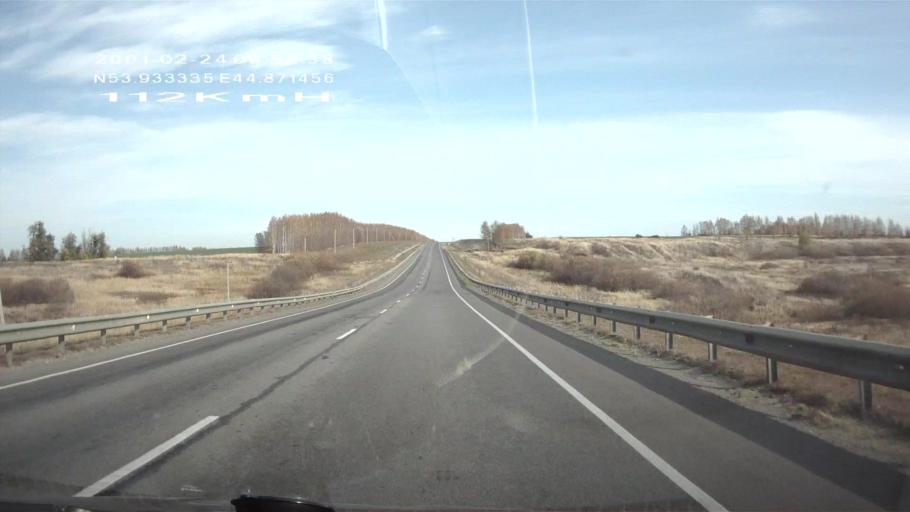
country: RU
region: Penza
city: Issa
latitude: 53.9338
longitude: 44.8718
